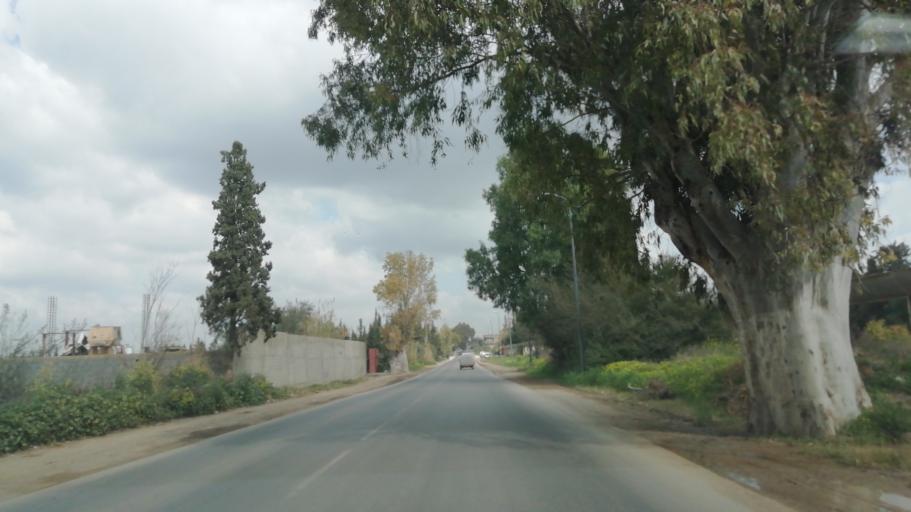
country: DZ
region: Mascara
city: Mascara
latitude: 35.6246
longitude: 0.1198
